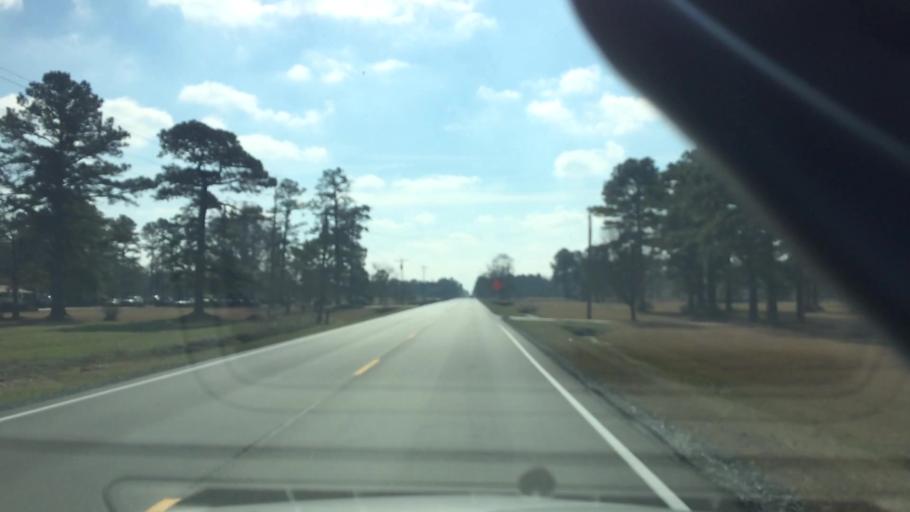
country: US
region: North Carolina
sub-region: Duplin County
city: Beulaville
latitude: 35.0229
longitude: -77.7497
